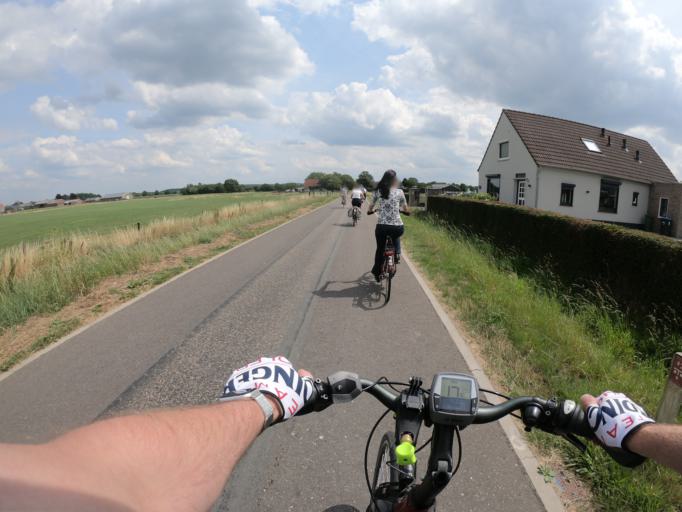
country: NL
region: Gelderland
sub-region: Gemeente Groesbeek
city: De Horst
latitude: 51.7709
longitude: 5.9536
